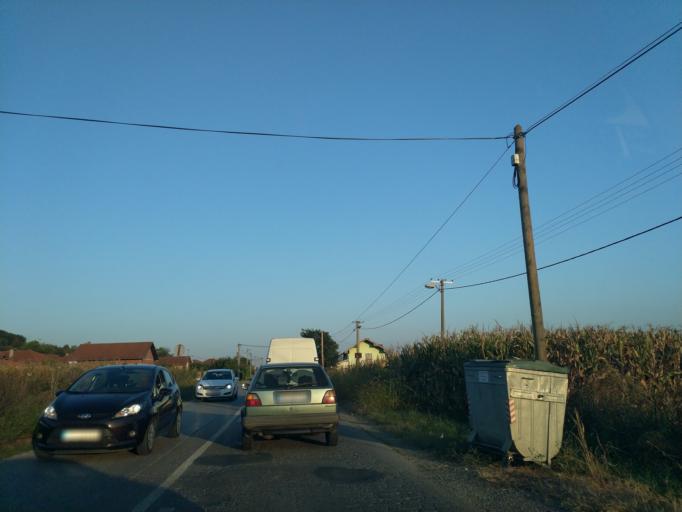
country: RS
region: Central Serbia
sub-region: Rasinski Okrug
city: Trstenik
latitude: 43.6311
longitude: 21.0383
